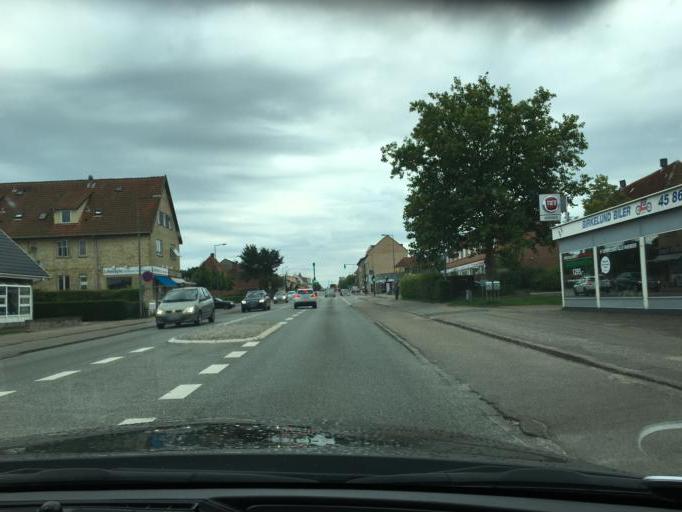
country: DK
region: Capital Region
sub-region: Horsholm Kommune
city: Horsholm
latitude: 55.8858
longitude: 12.4975
